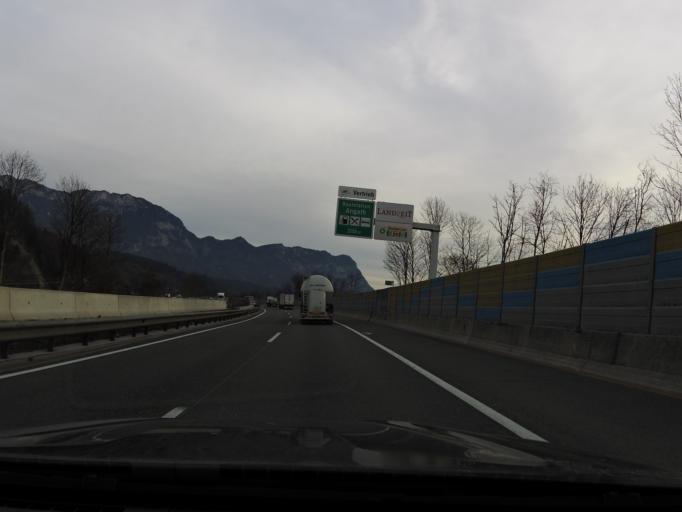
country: AT
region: Tyrol
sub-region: Politischer Bezirk Kufstein
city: Angath
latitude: 47.4945
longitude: 12.0577
